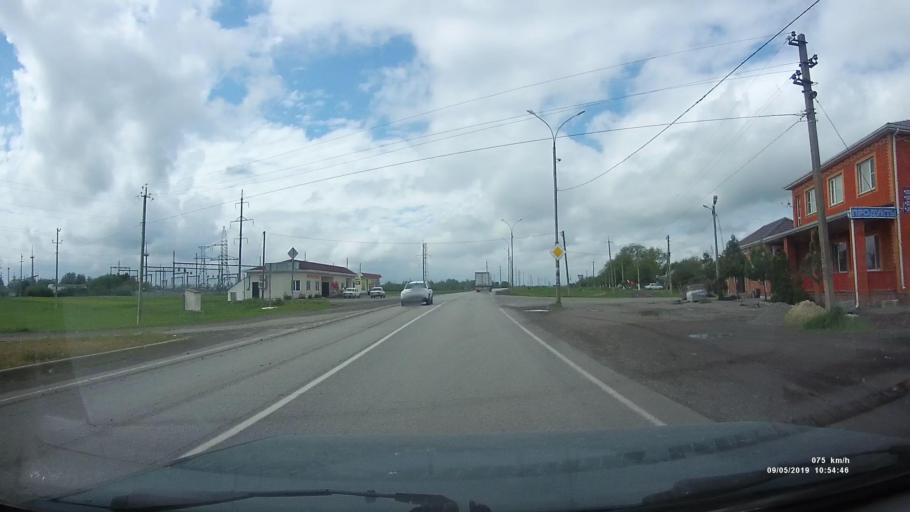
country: RU
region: Rostov
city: Peshkovo
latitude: 46.8756
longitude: 39.3255
